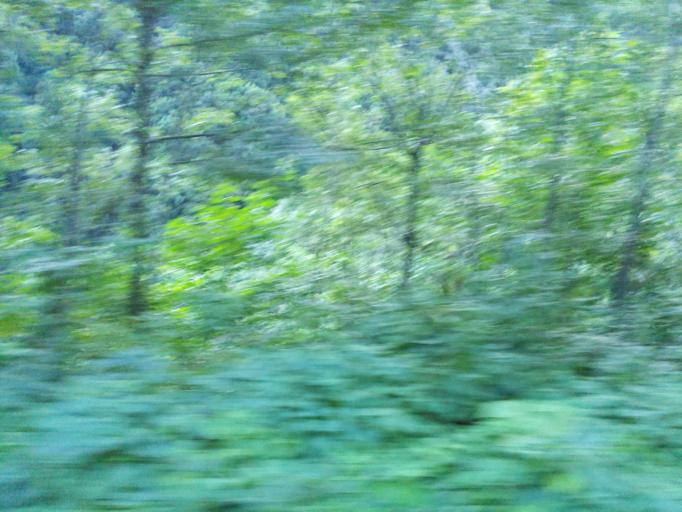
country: JP
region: Toyama
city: Kamiichi
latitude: 36.5230
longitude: 137.4499
